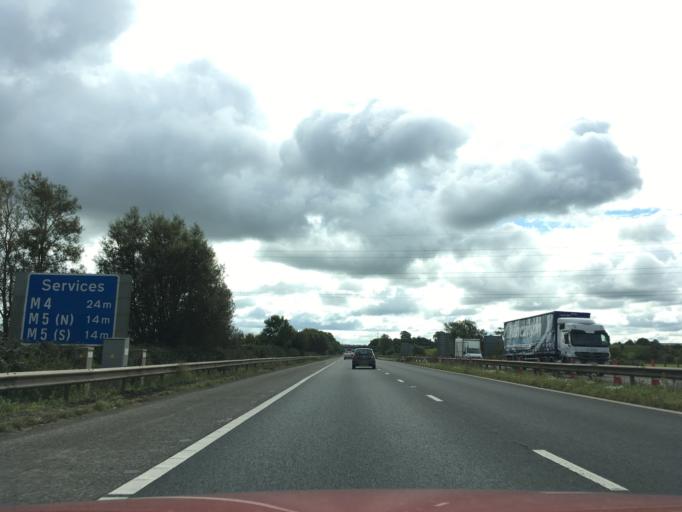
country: GB
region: England
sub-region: South Gloucestershire
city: Almondsbury
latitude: 51.5949
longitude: -2.6063
